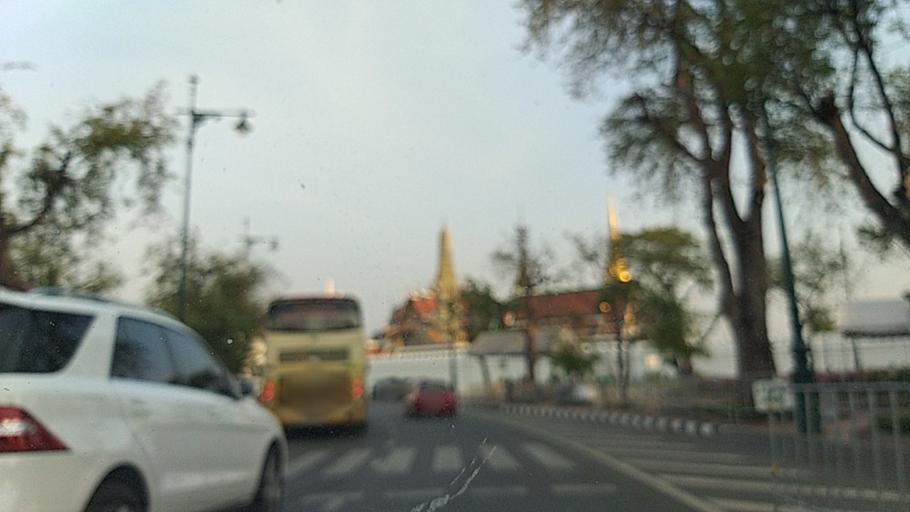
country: TH
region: Bangkok
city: Bangkok
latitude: 13.7530
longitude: 100.4917
